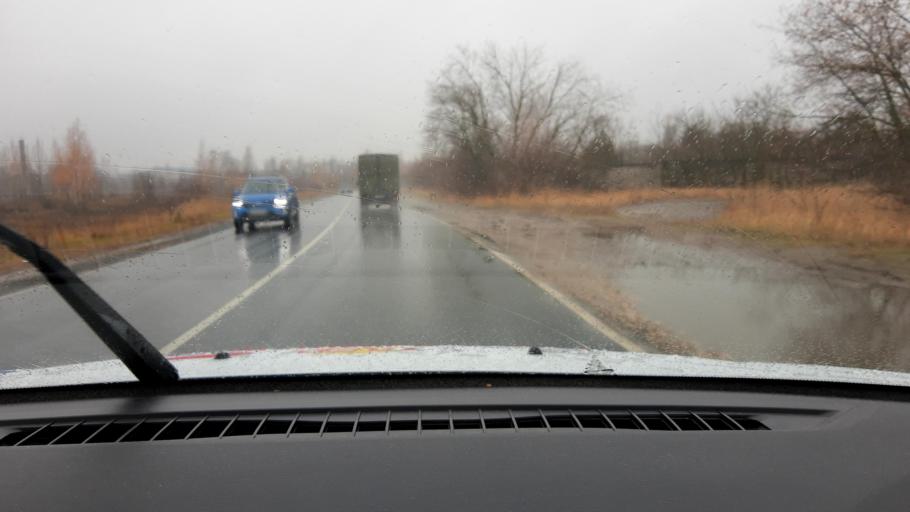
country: RU
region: Nizjnij Novgorod
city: Babino
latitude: 56.2596
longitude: 43.6556
